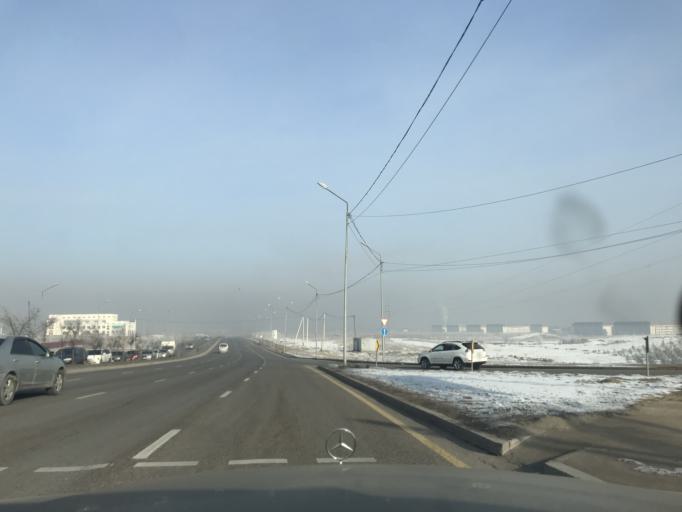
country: KZ
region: Almaty Oblysy
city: Burunday
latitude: 43.3135
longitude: 76.8341
